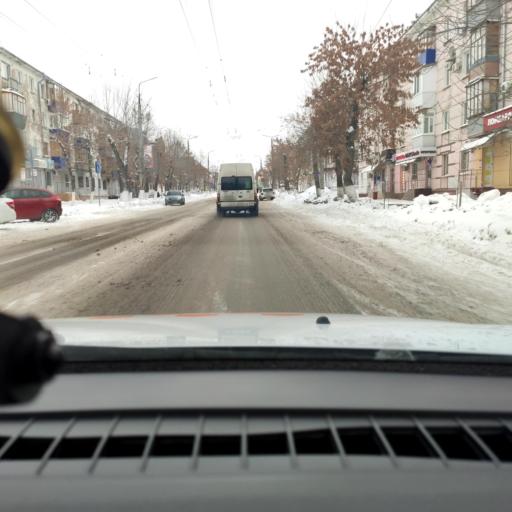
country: RU
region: Samara
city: Novokuybyshevsk
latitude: 53.0924
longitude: 49.9500
